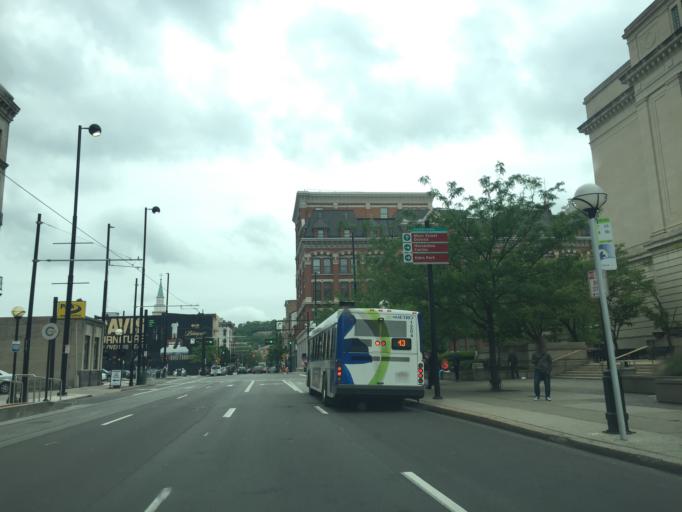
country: US
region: Kentucky
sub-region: Campbell County
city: Newport
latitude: 39.1069
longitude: -84.5110
